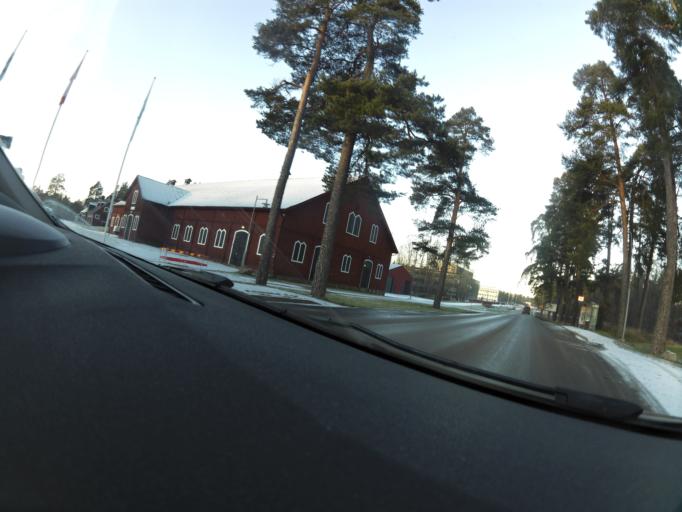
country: SE
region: Gaevleborg
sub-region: Gavle Kommun
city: Gavle
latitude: 60.6684
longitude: 17.1102
